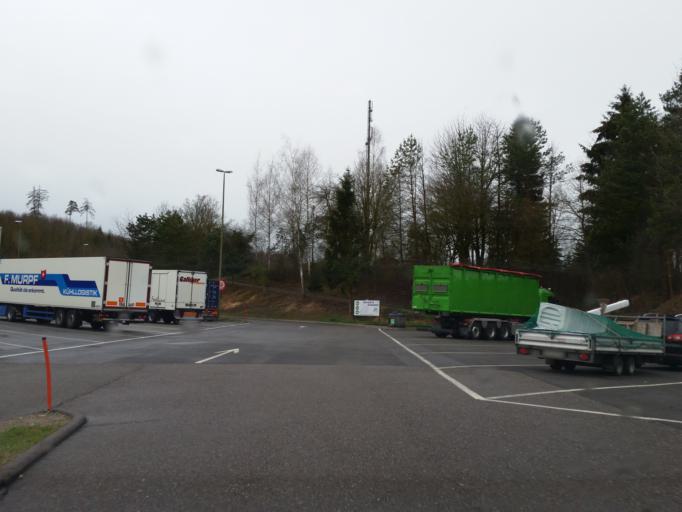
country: CH
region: Zurich
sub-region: Bezirk Winterthur
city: Seuzach Dorf / Breite-Weid
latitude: 47.5268
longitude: 8.7335
